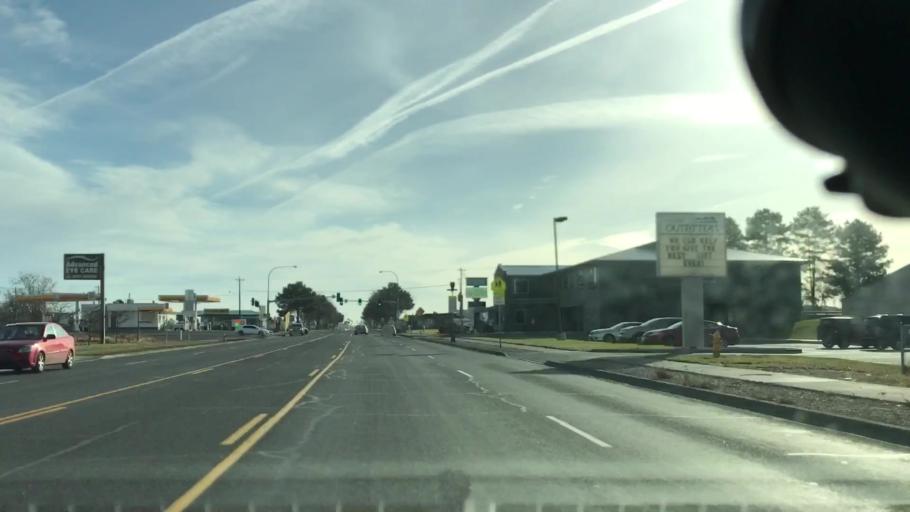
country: US
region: Washington
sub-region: Grant County
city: Moses Lake
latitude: 47.1176
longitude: -119.2654
